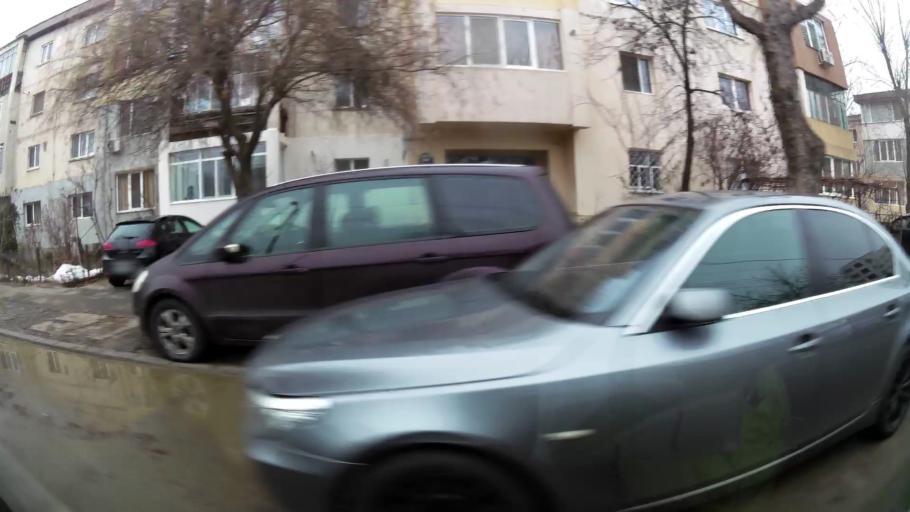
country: RO
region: Ilfov
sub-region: Comuna Chiajna
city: Rosu
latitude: 44.4389
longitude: 26.0032
